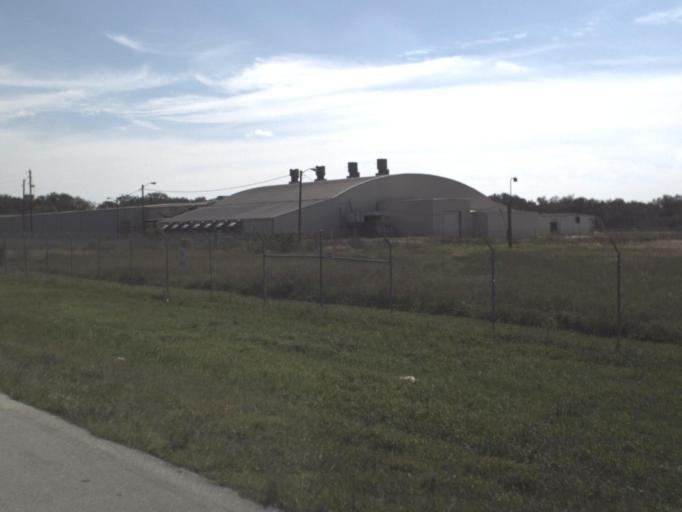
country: US
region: Florida
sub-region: Highlands County
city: Avon Park
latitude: 27.5956
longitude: -81.5229
